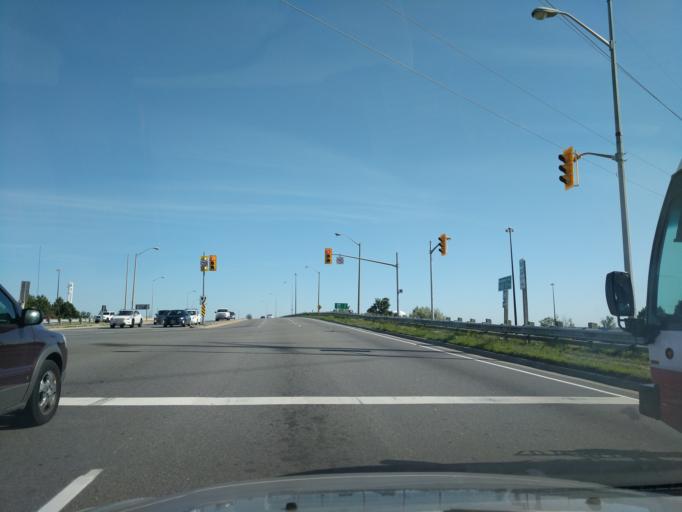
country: CA
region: Ontario
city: Scarborough
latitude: 43.7947
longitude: -79.1963
